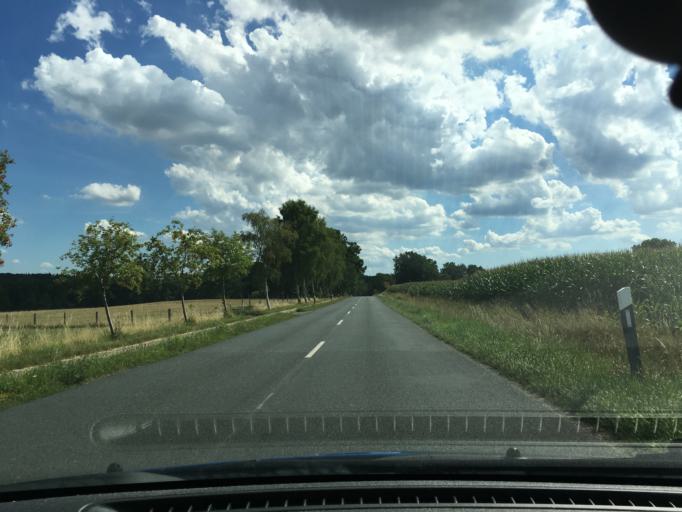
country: DE
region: Lower Saxony
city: Rehlingen
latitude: 53.1118
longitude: 10.2182
